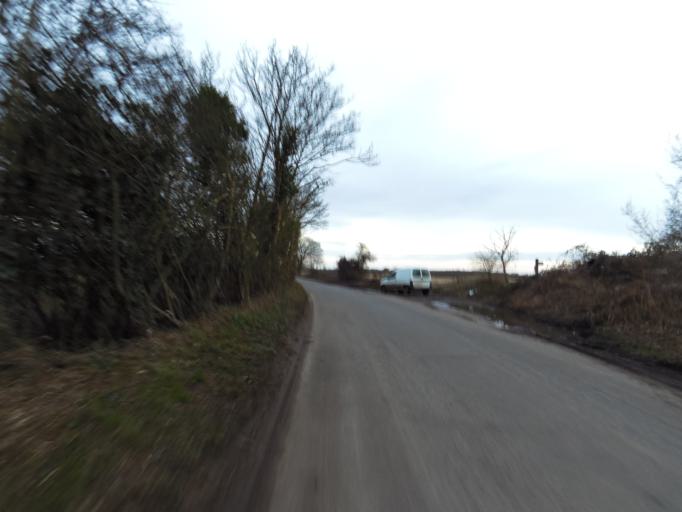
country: GB
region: England
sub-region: Suffolk
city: Ipswich
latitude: 52.0175
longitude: 1.1169
